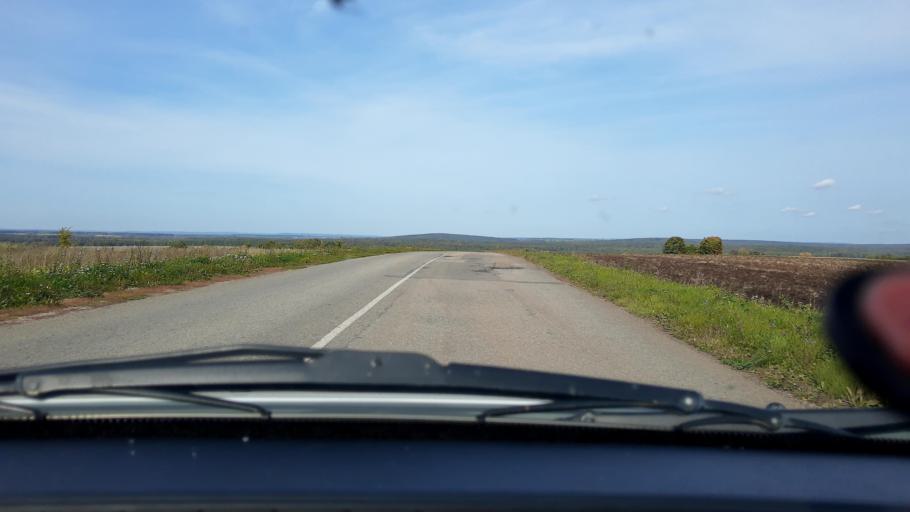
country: RU
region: Bashkortostan
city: Iglino
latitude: 54.7667
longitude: 56.5528
